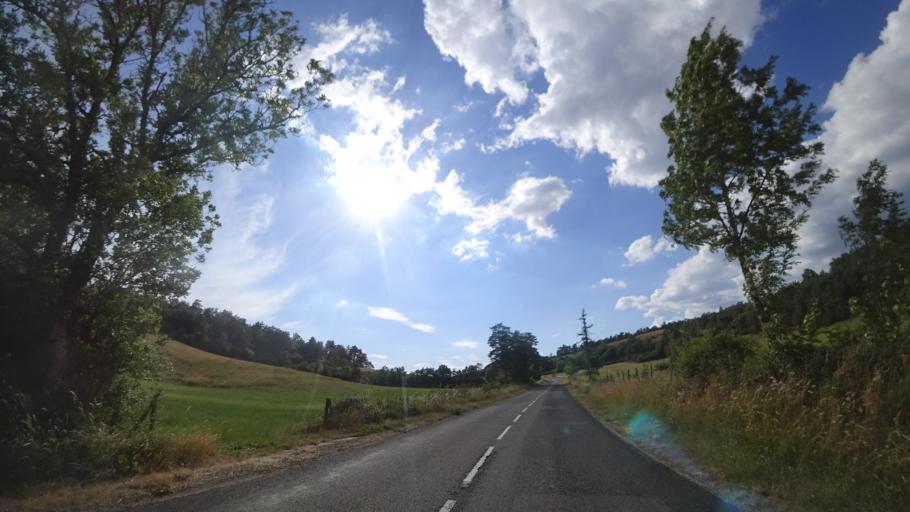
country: FR
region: Languedoc-Roussillon
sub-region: Departement de la Lozere
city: Chanac
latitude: 44.3758
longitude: 3.3295
